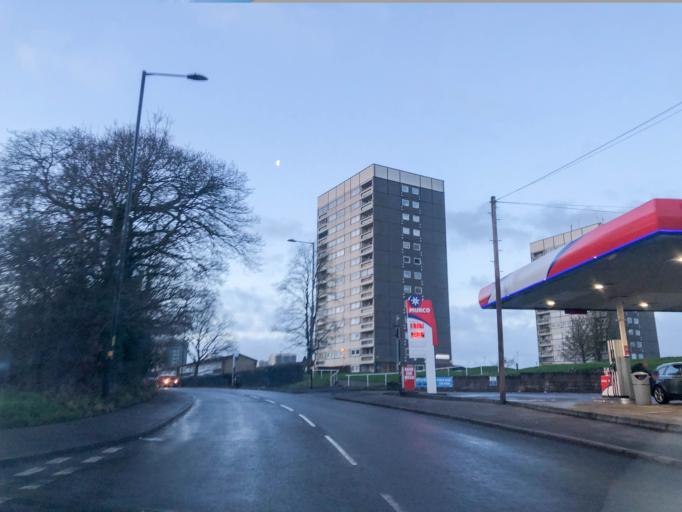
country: GB
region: England
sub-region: Solihull
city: Tidbury Green
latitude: 52.4104
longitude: -1.8865
